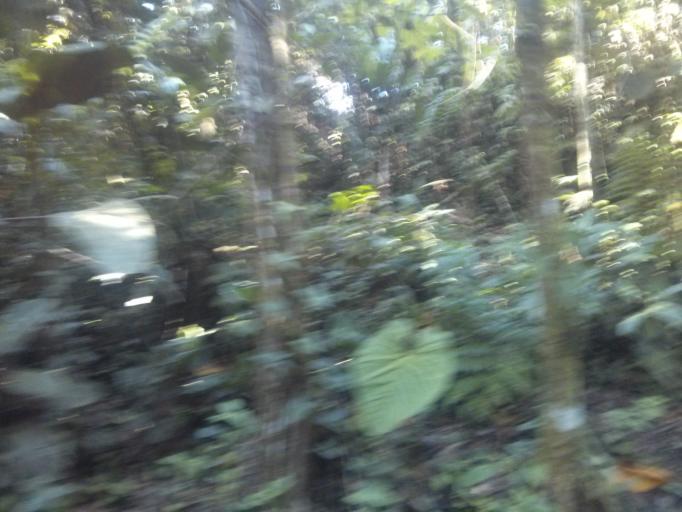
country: CR
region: Cartago
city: Turrialba
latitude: 9.9712
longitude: -83.6908
